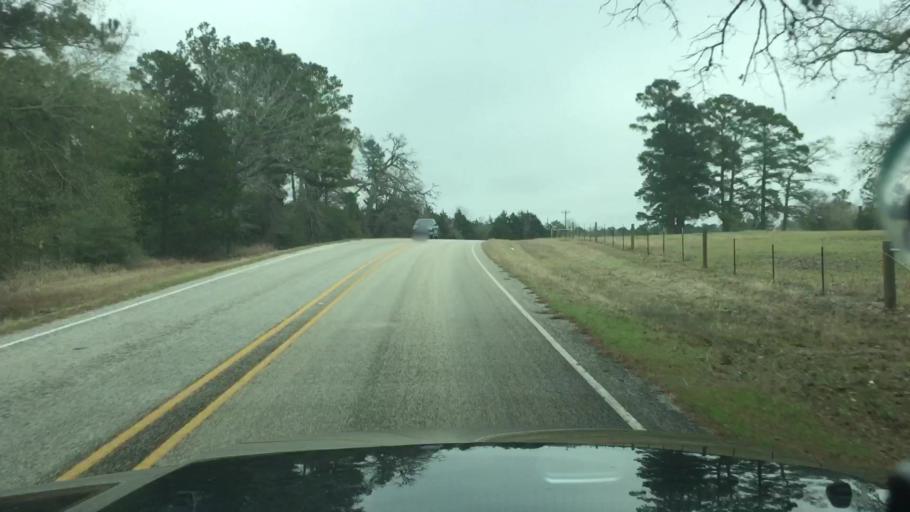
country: US
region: Texas
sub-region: Fayette County
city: La Grange
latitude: 30.0127
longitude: -96.9335
